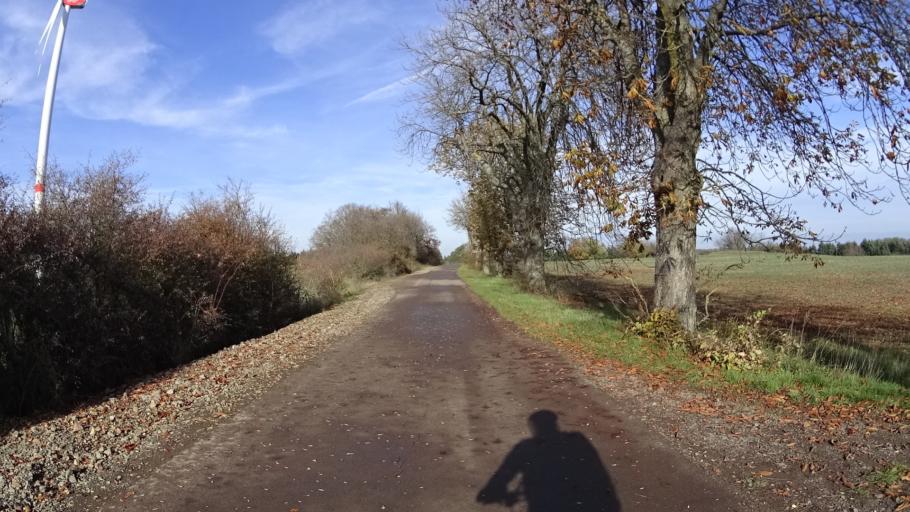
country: DE
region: Rheinland-Pfalz
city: Kirrweiler
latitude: 49.6463
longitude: 7.4951
